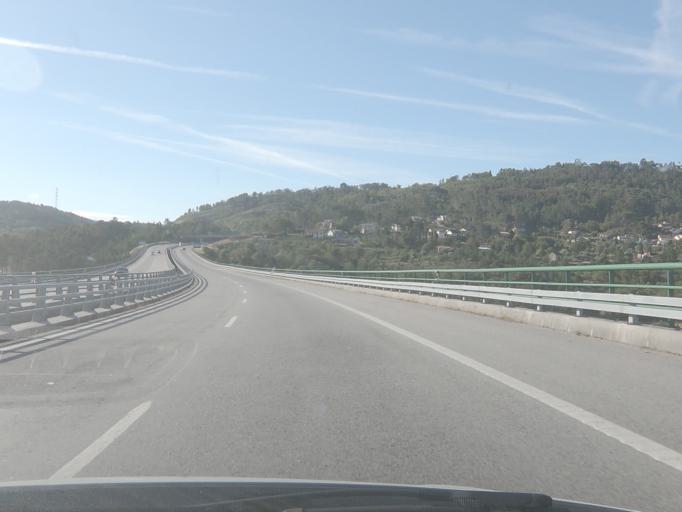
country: PT
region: Viseu
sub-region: Viseu
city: Campo
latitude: 40.7981
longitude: -7.9281
